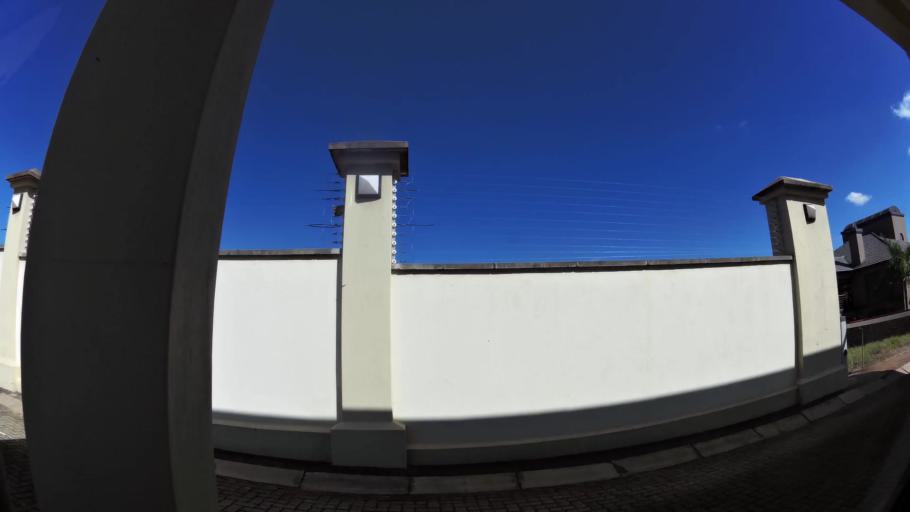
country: ZA
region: Limpopo
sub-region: Mopani District Municipality
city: Tzaneen
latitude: -23.8165
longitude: 30.1689
